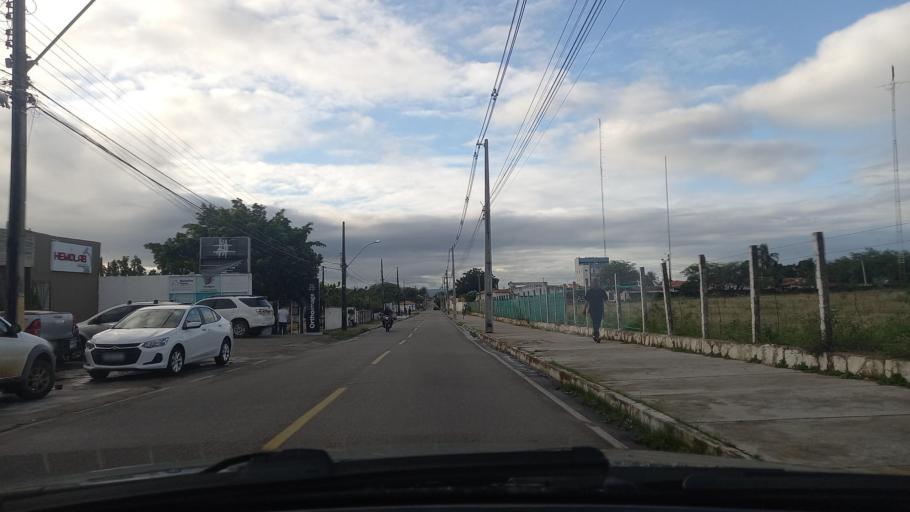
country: BR
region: Bahia
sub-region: Paulo Afonso
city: Paulo Afonso
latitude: -9.3969
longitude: -38.2316
